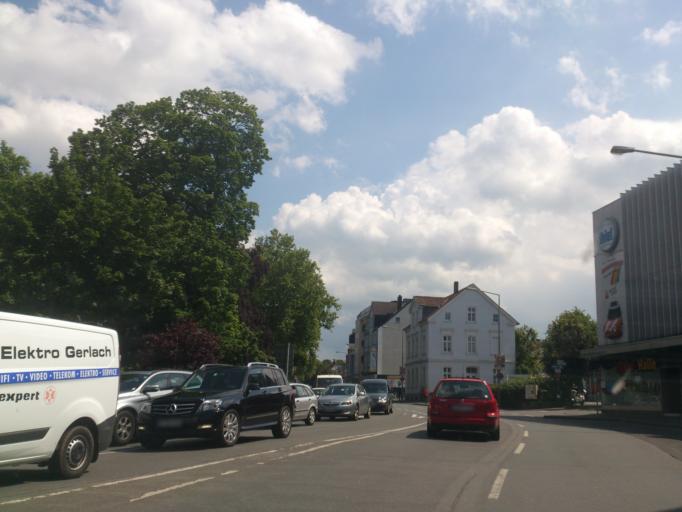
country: DE
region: North Rhine-Westphalia
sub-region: Regierungsbezirk Detmold
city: Paderborn
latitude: 51.7154
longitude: 8.7467
